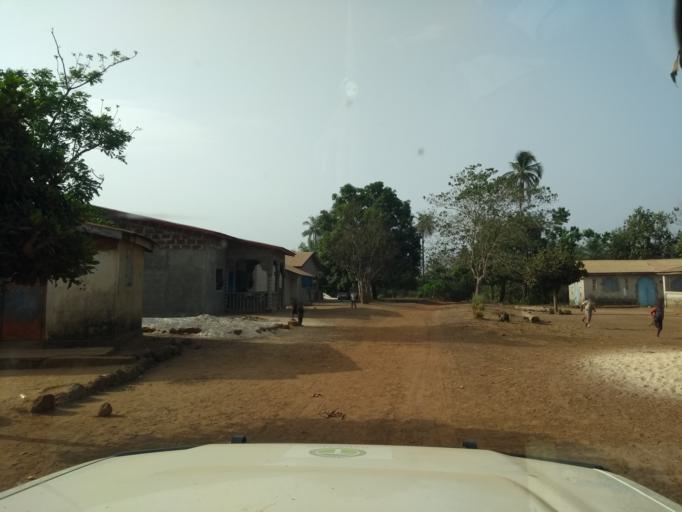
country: GN
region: Kindia
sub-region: Prefecture de Dubreka
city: Dubreka
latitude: 9.8426
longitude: -13.5607
